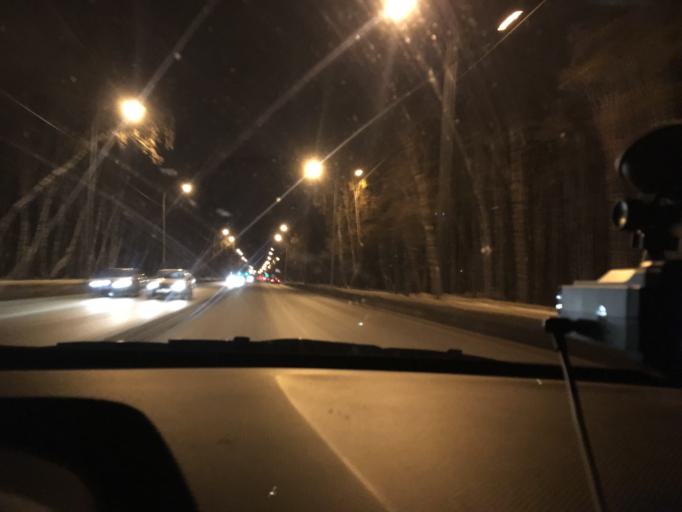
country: RU
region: Tjumen
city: Melioratorov
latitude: 57.1785
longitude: 65.5971
